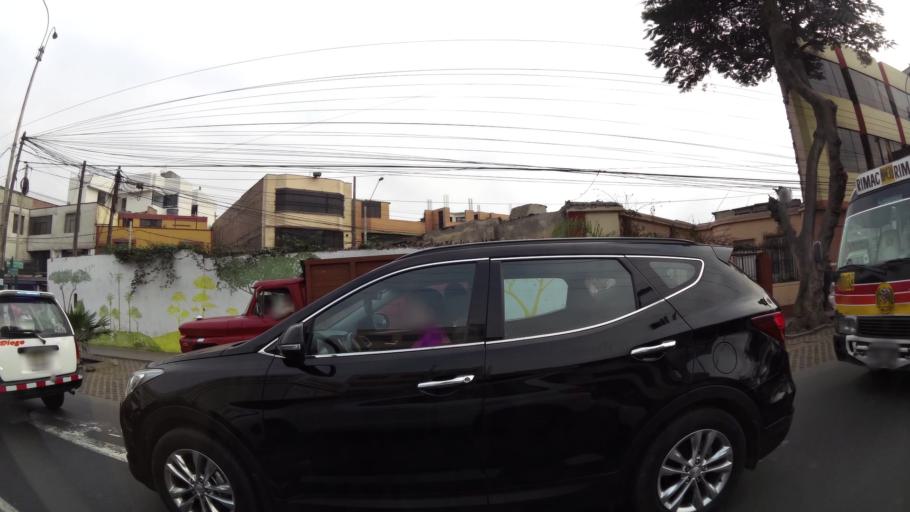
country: PE
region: Lima
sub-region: Lima
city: Surco
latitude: -12.1468
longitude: -77.0121
